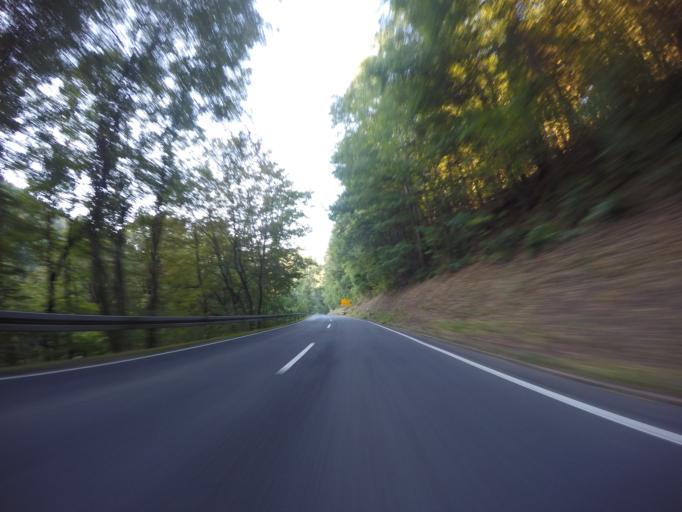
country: DE
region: Bavaria
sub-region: Regierungsbezirk Unterfranken
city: Hasloch
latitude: 49.8194
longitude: 9.4953
